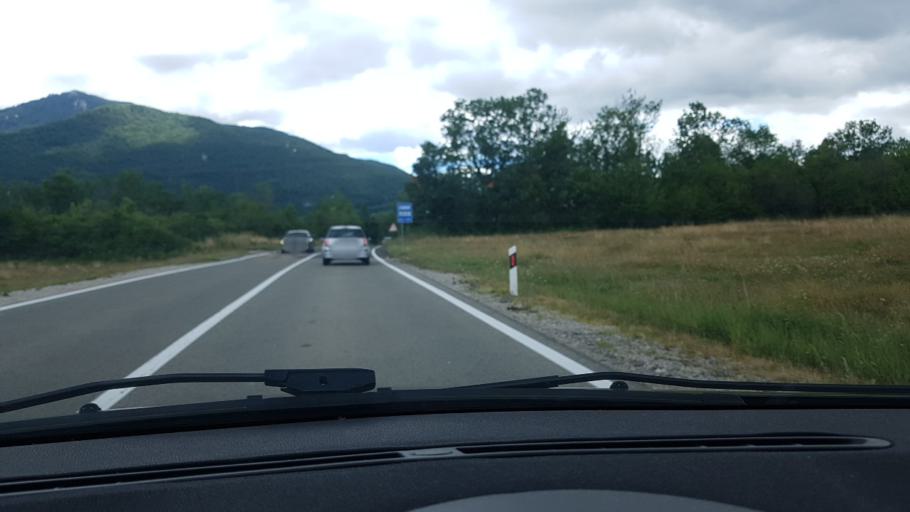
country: HR
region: Zadarska
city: Gracac
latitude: 44.2980
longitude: 15.8584
